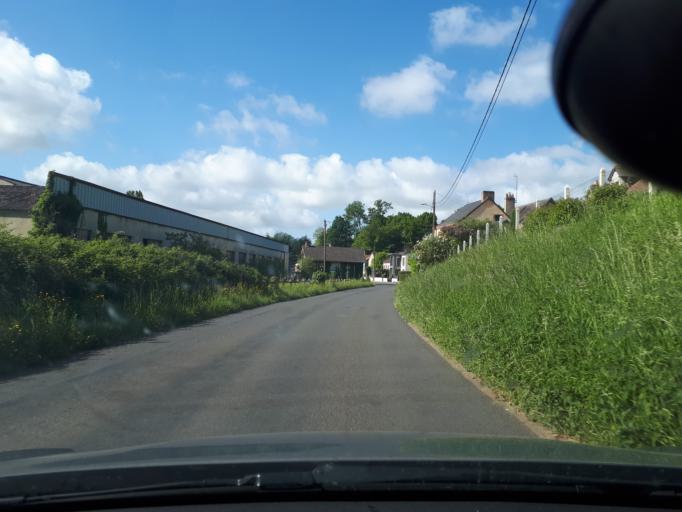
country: FR
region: Pays de la Loire
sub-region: Departement de la Sarthe
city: Change
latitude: 48.0218
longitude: 0.2765
